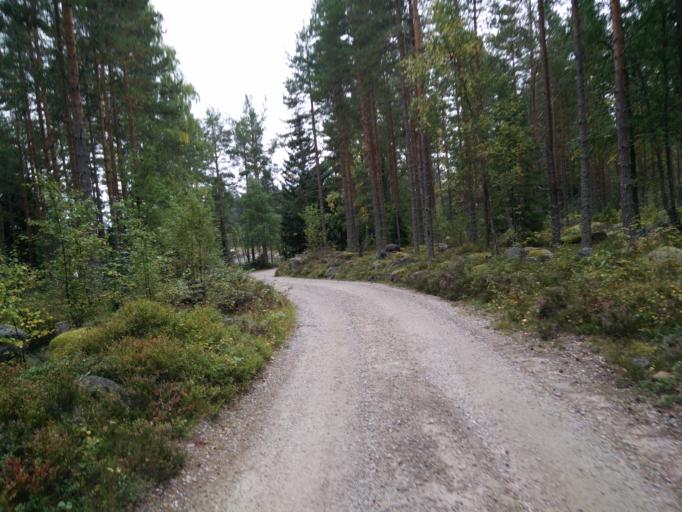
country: SE
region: Gaevleborg
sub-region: Hudiksvalls Kommun
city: Hudiksvall
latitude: 61.8339
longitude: 17.3389
